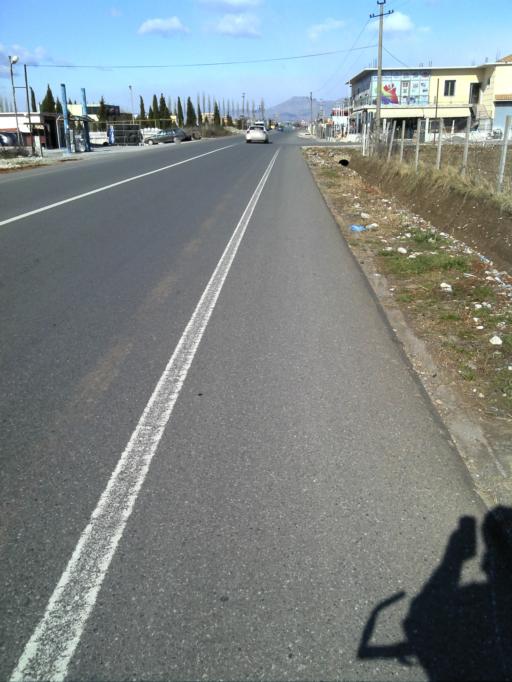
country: AL
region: Shkoder
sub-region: Rrethi i Shkodres
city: Shkoder
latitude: 42.0926
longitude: 19.5066
